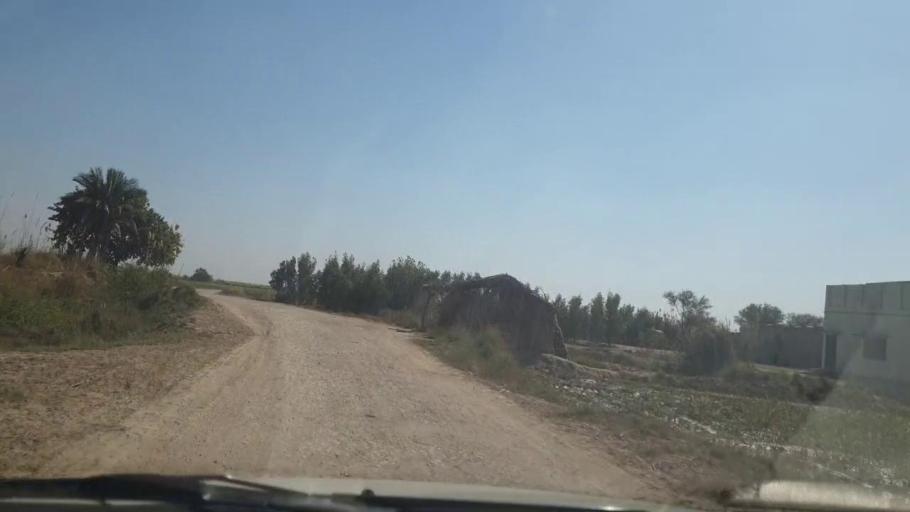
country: PK
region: Sindh
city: Mirpur Khas
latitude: 25.4942
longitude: 69.1369
